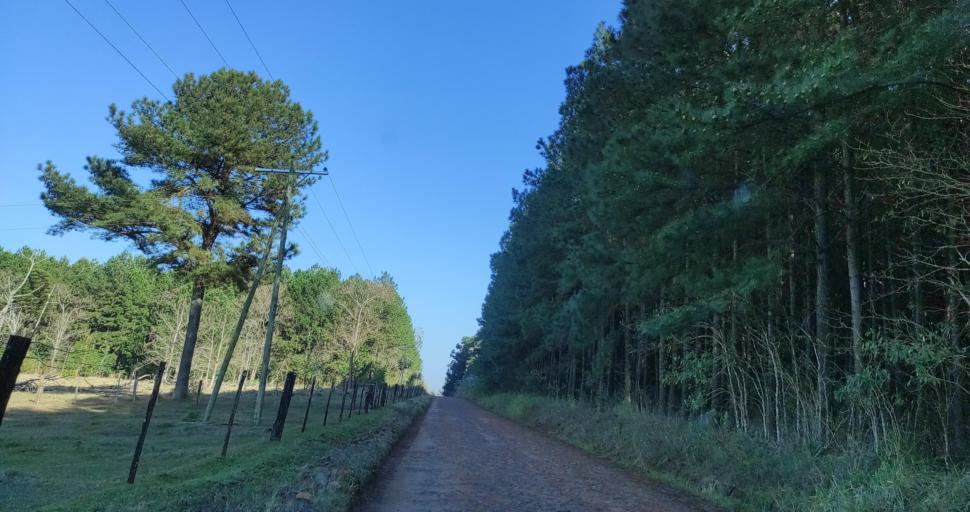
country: AR
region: Misiones
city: Puerto Rico
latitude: -26.8618
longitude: -55.0186
